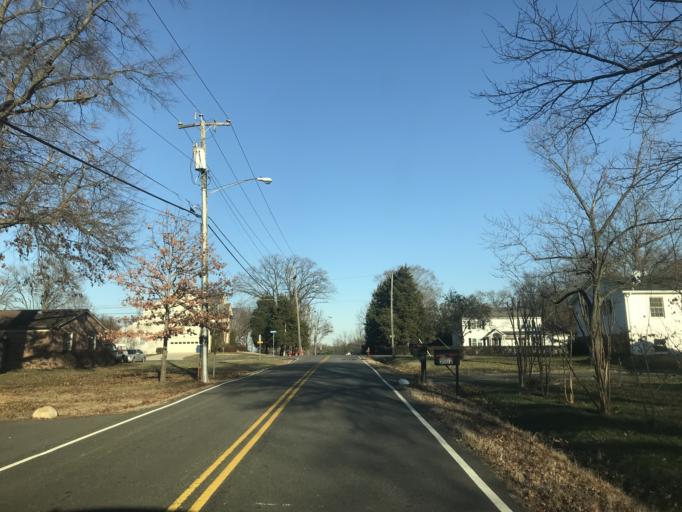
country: US
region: Virginia
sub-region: Fairfax County
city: Franconia
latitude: 38.7909
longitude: -77.1510
